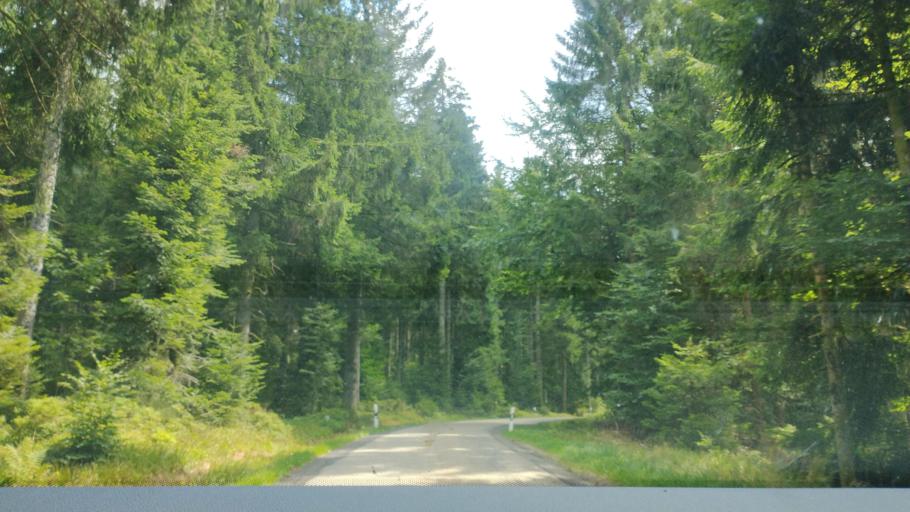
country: DE
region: Baden-Wuerttemberg
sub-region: Freiburg Region
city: Oppenau
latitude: 48.4406
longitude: 8.1465
